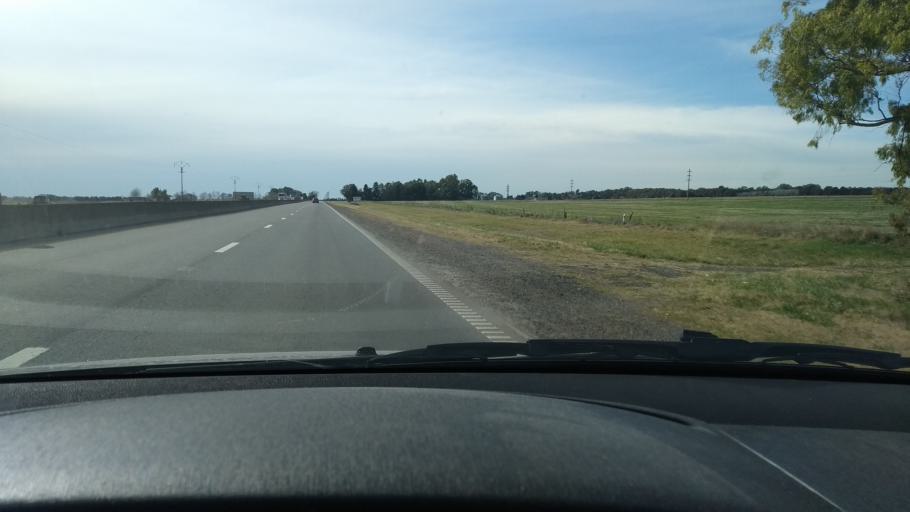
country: AR
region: Buenos Aires
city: Olavarria
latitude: -36.9086
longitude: -60.1946
